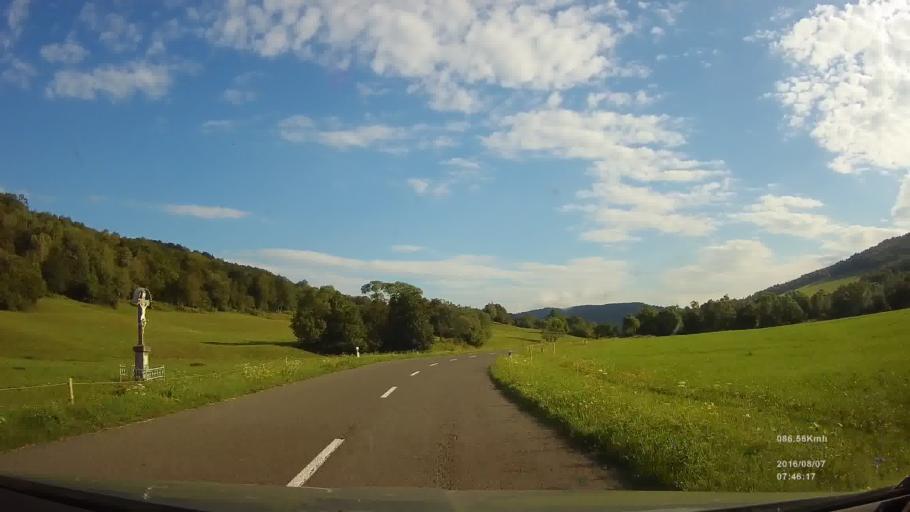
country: SK
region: Presovsky
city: Stropkov
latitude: 49.2678
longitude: 21.7483
